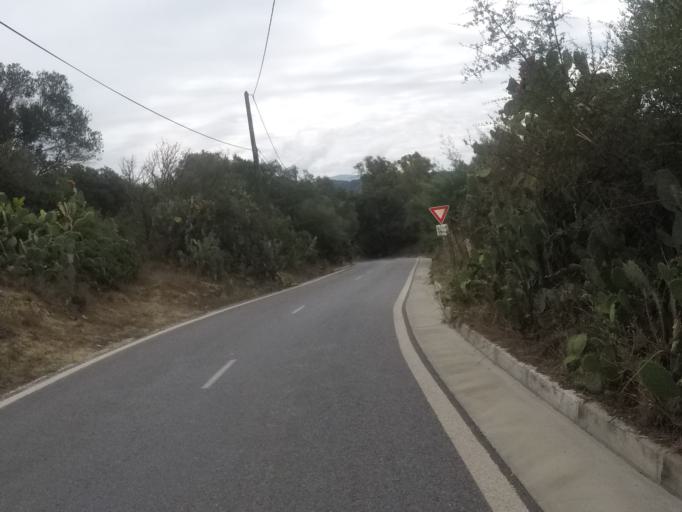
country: FR
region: Corsica
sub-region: Departement de la Corse-du-Sud
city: Propriano
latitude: 41.7294
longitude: 8.8290
